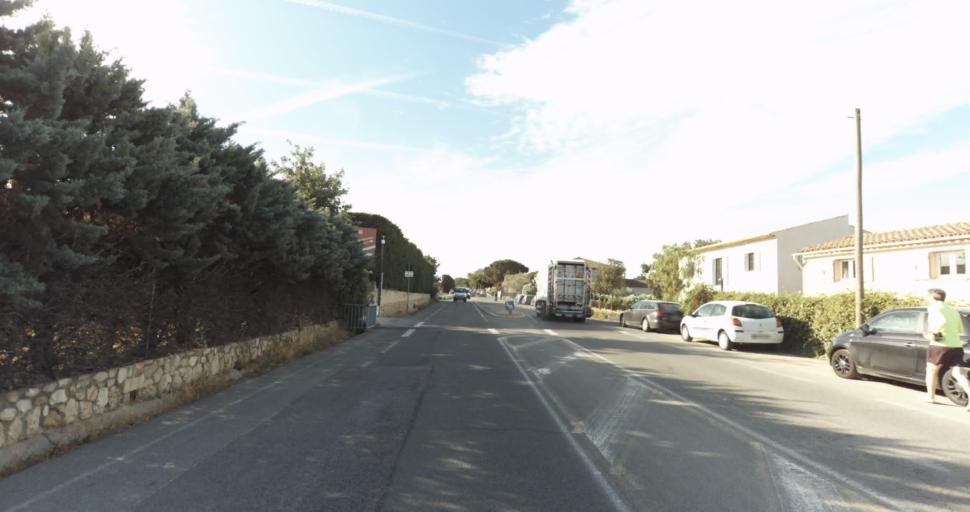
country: FR
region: Provence-Alpes-Cote d'Azur
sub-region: Departement du Var
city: Saint-Tropez
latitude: 43.2595
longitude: 6.6318
